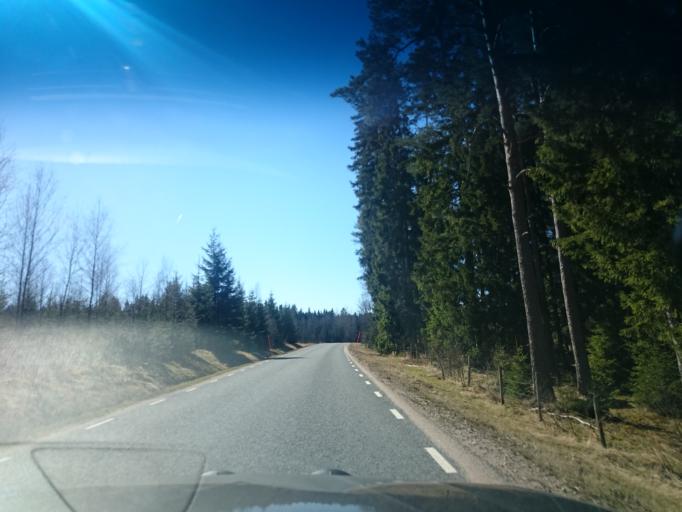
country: SE
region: Joenkoeping
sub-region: Vetlanda Kommun
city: Vetlanda
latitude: 57.2612
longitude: 15.0792
